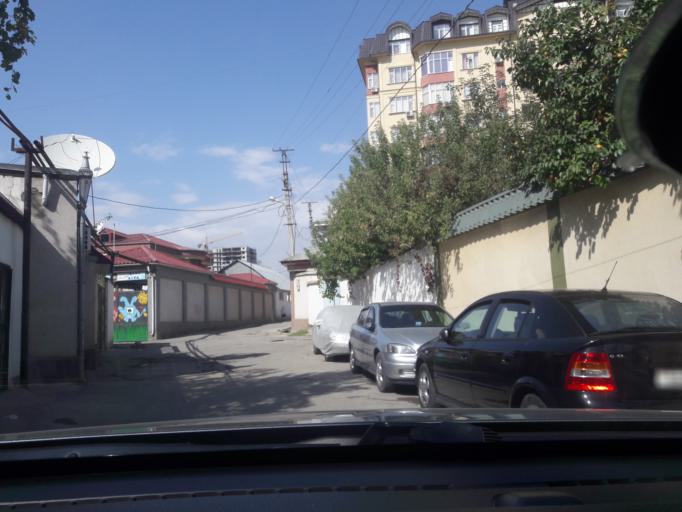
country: TJ
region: Dushanbe
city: Dushanbe
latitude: 38.5750
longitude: 68.7970
